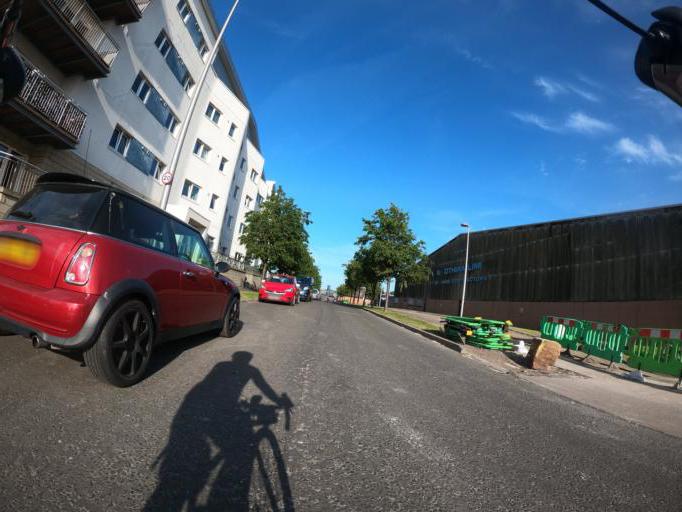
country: GB
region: Scotland
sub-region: Edinburgh
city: Edinburgh
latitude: 55.9835
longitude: -3.2250
